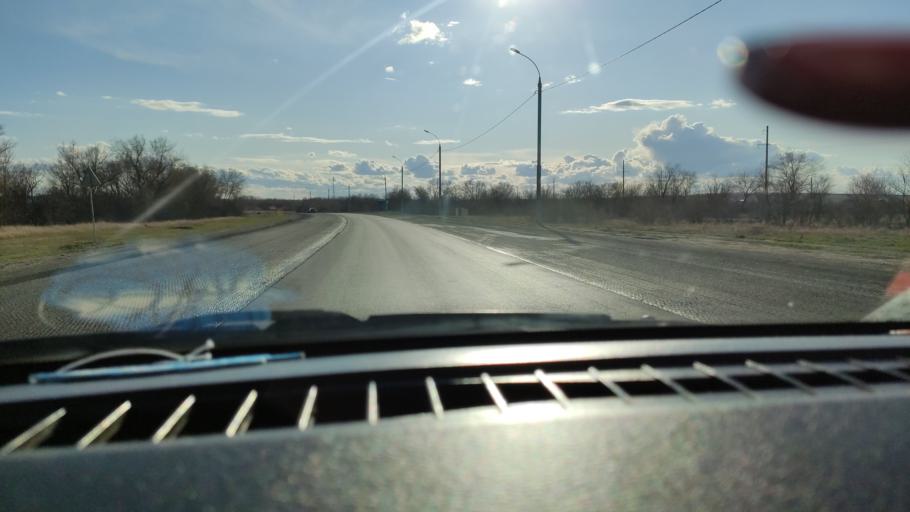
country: RU
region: Saratov
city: Yelshanka
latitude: 51.8278
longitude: 46.2241
